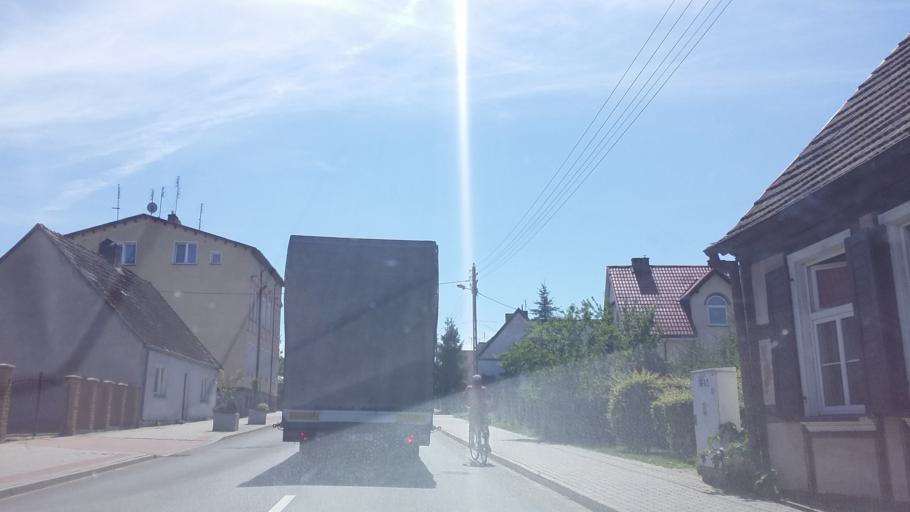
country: PL
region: West Pomeranian Voivodeship
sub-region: Powiat lobeski
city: Lobez
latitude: 53.6379
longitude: 15.6255
